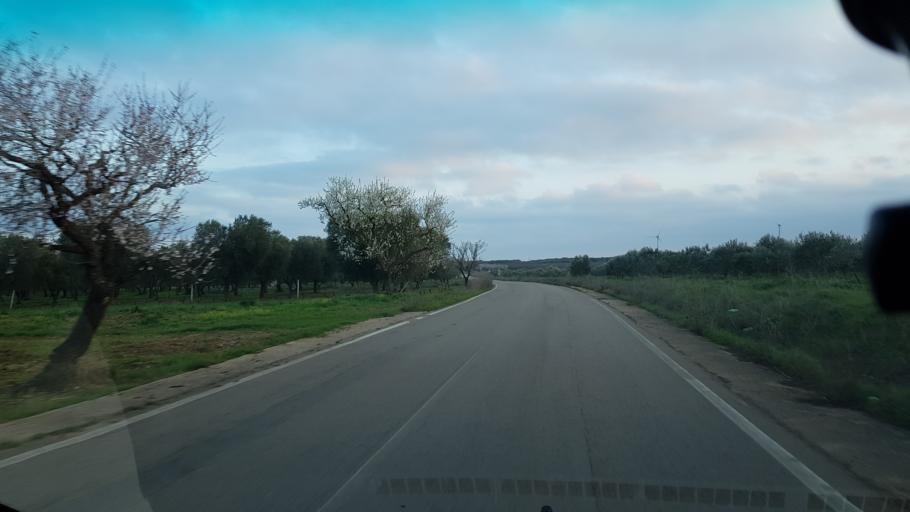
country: IT
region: Apulia
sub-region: Provincia di Brindisi
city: Mesagne
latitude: 40.6229
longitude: 17.7839
